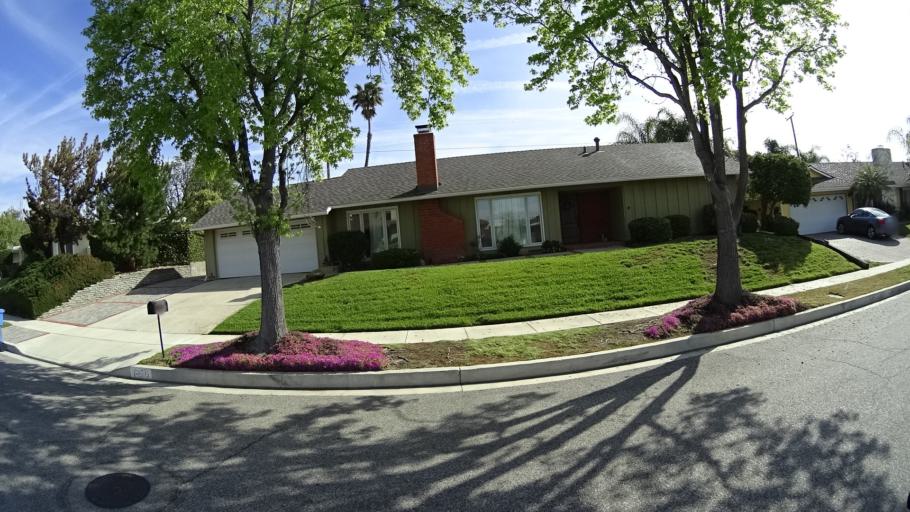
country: US
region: California
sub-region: Ventura County
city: Thousand Oaks
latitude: 34.1986
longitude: -118.8807
